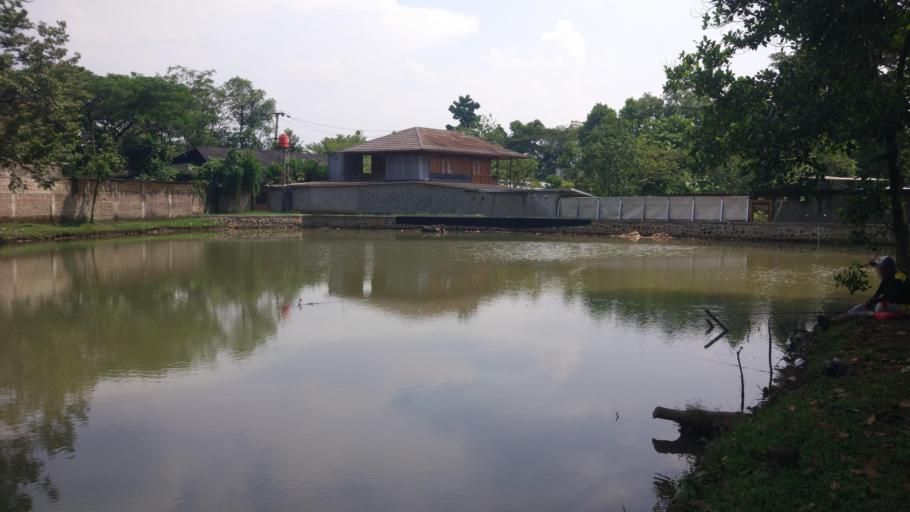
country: ID
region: West Java
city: Ciampea
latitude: -6.5579
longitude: 106.7508
